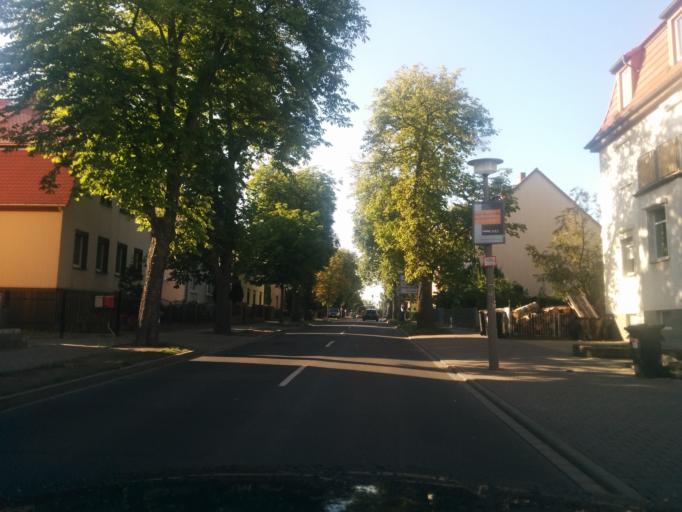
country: DE
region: Saxony-Anhalt
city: Halle Neustadt
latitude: 51.4870
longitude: 11.9078
